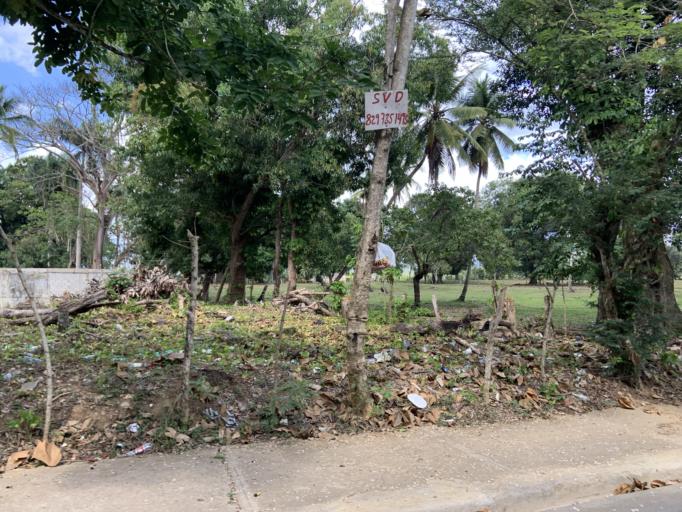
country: DO
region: Monte Plata
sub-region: Yamasa
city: Yamasa
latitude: 18.7708
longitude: -70.0182
